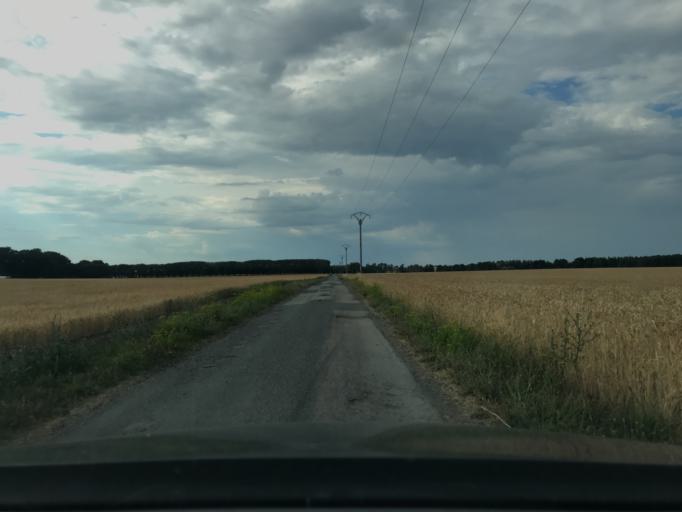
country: SE
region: Skane
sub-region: Simrishamns Kommun
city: Kivik
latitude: 55.5340
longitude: 14.1568
